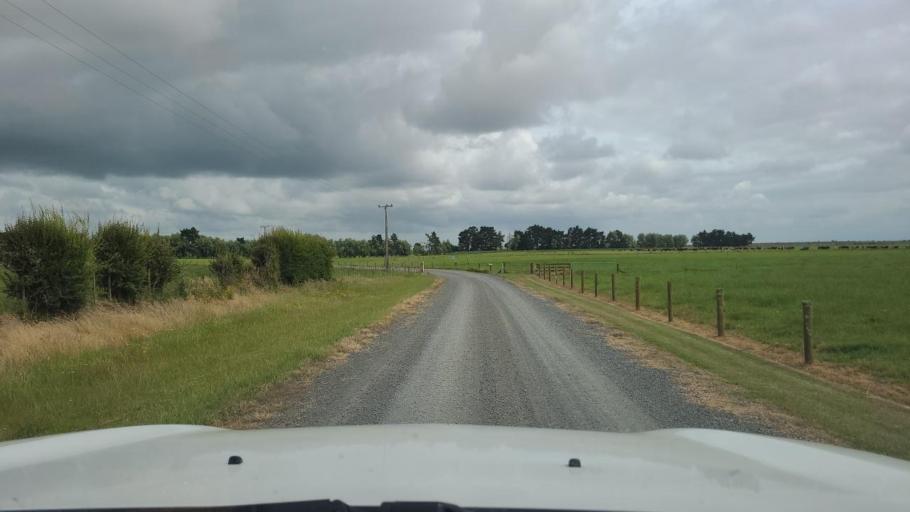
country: NZ
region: Waikato
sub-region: Hauraki District
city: Paeroa
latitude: -37.5068
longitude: 175.5880
